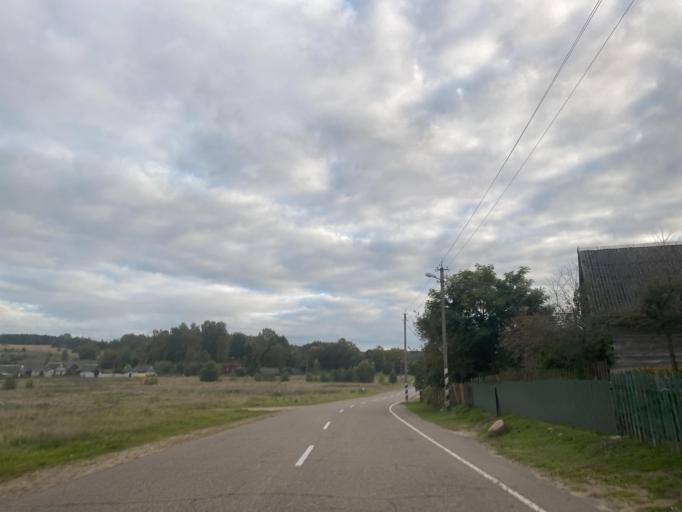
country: BY
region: Grodnenskaya
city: Kreva
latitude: 54.3067
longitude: 26.2791
